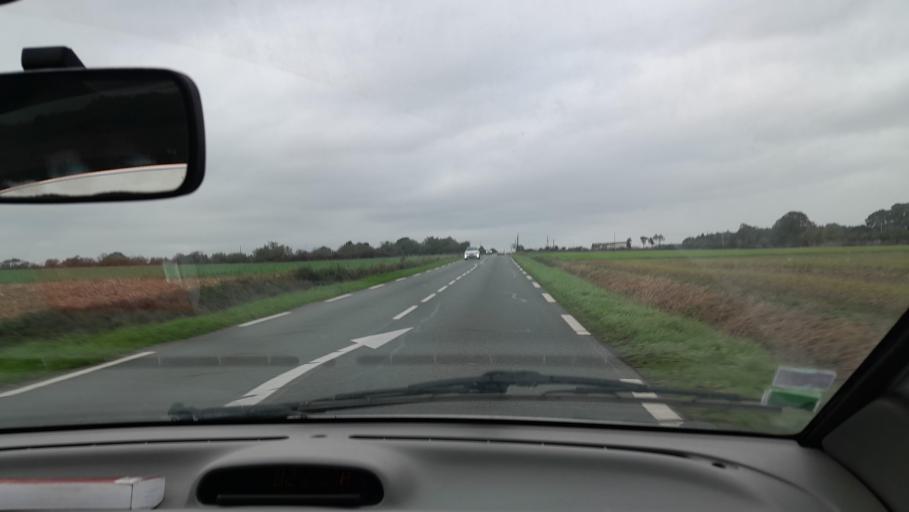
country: FR
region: Pays de la Loire
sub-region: Departement de la Loire-Atlantique
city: Saint-Mars-la-Jaille
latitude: 47.5679
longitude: -1.1876
